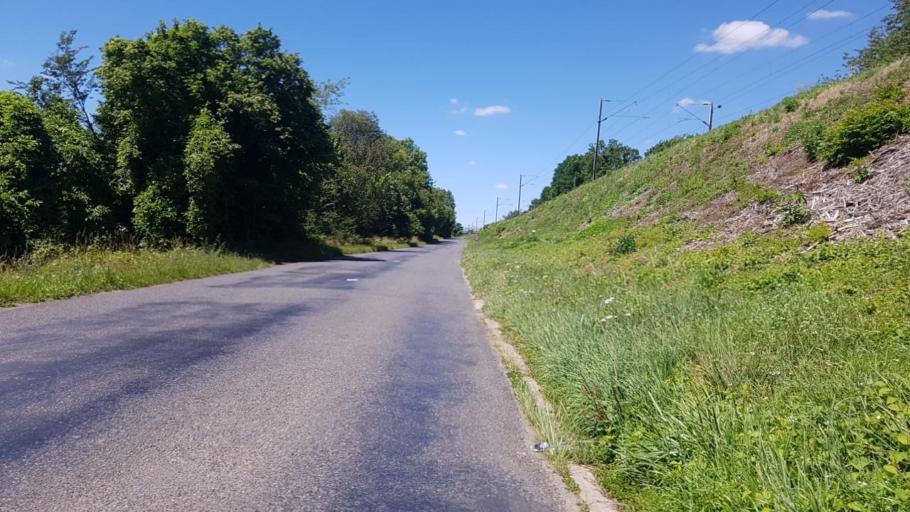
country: FR
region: Ile-de-France
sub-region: Departement de Seine-et-Marne
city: Changis-sur-Marne
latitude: 48.9590
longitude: 3.0354
